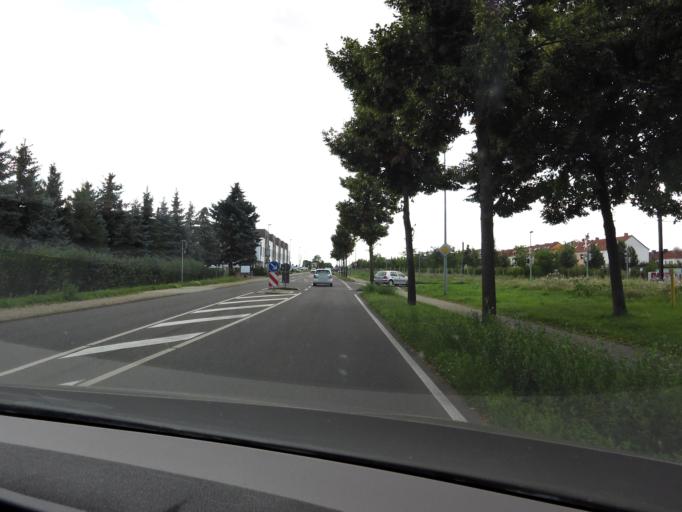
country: DE
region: Saxony-Anhalt
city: Magdeburg
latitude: 52.0851
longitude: 11.6214
